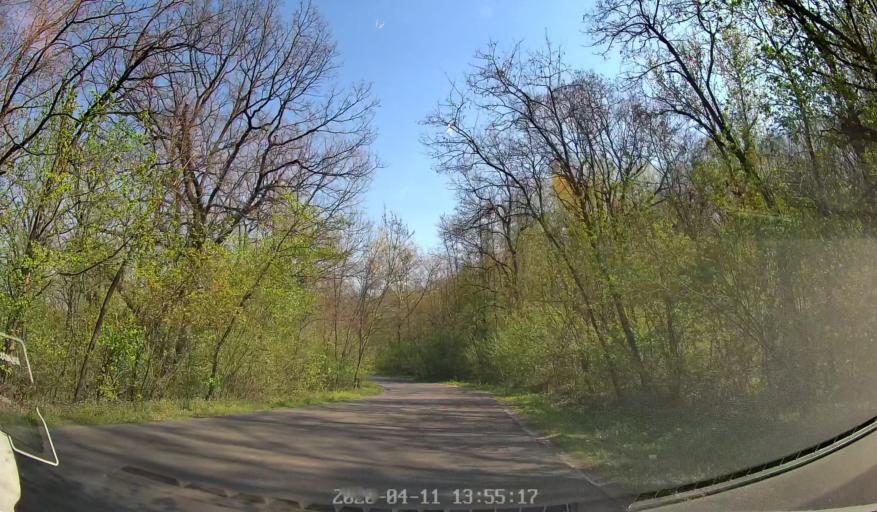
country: MD
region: Chisinau
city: Vadul lui Voda
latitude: 47.0721
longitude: 29.1117
